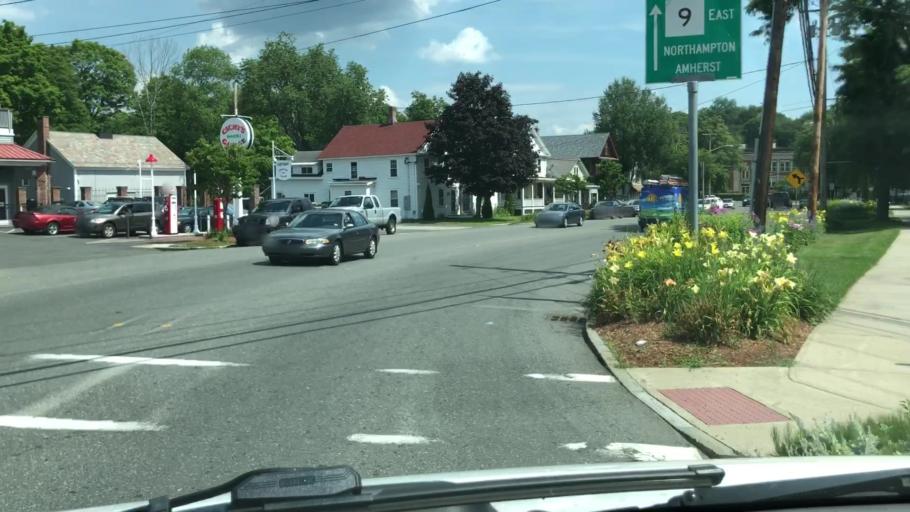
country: US
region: Massachusetts
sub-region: Hampshire County
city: Williamsburg
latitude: 42.3926
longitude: -72.7302
